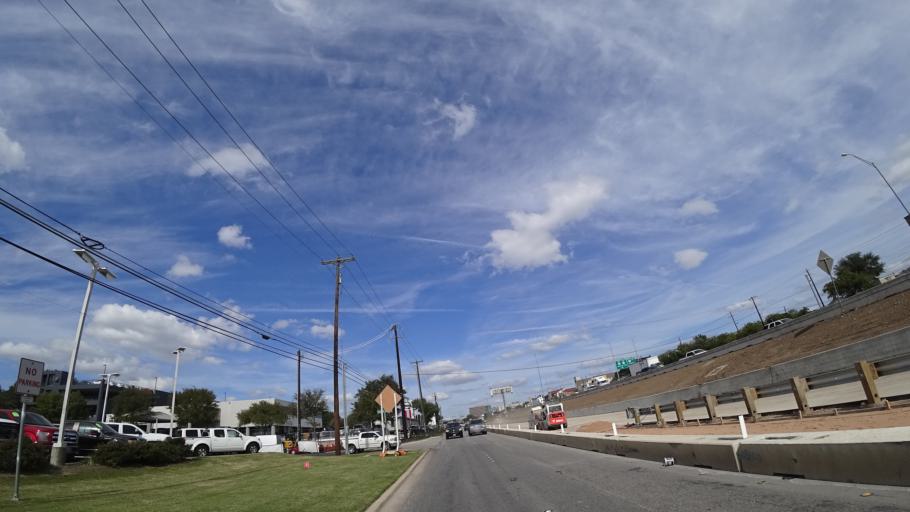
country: US
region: Texas
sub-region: Travis County
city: Austin
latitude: 30.2053
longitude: -97.7591
